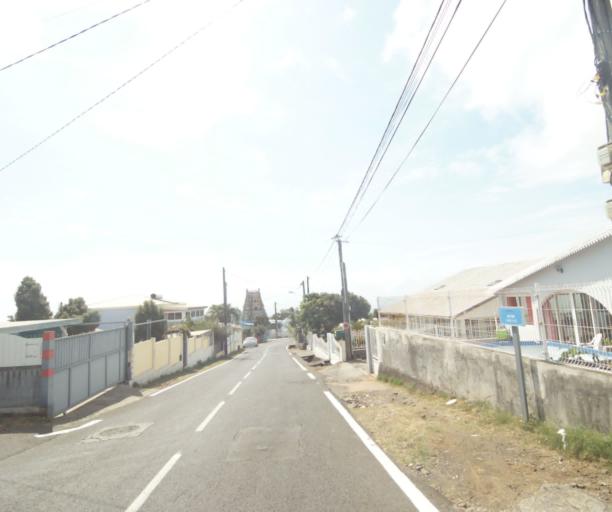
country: RE
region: Reunion
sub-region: Reunion
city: Saint-Paul
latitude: -21.0461
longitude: 55.2637
